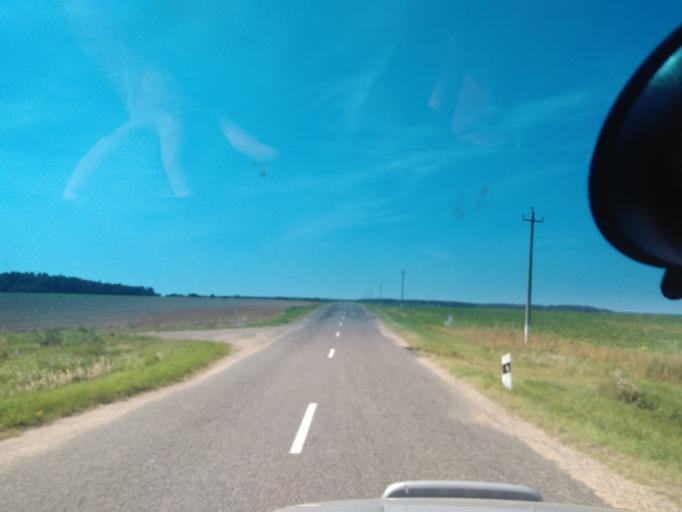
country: BY
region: Minsk
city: Kapyl'
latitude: 53.2179
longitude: 27.1436
